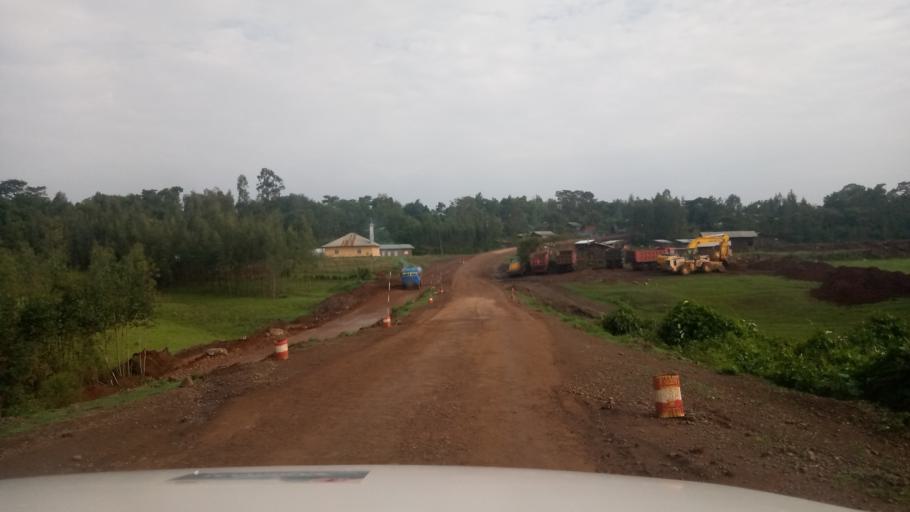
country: ET
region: Oromiya
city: Agaro
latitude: 7.8563
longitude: 36.6531
